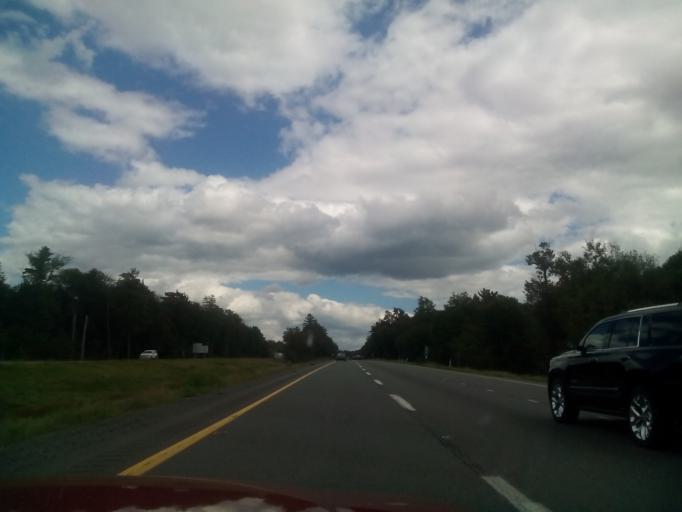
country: US
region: Pennsylvania
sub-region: Carbon County
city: Towamensing Trails
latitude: 41.0764
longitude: -75.5711
